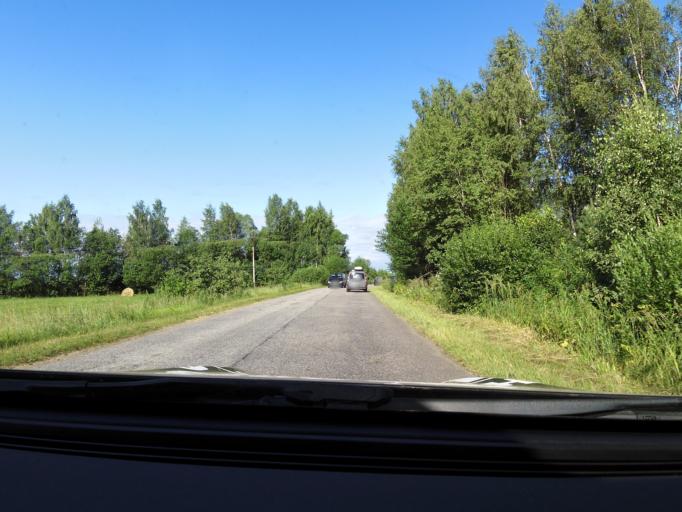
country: RU
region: Tverskaya
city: Zavidovo
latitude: 56.6090
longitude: 36.5620
